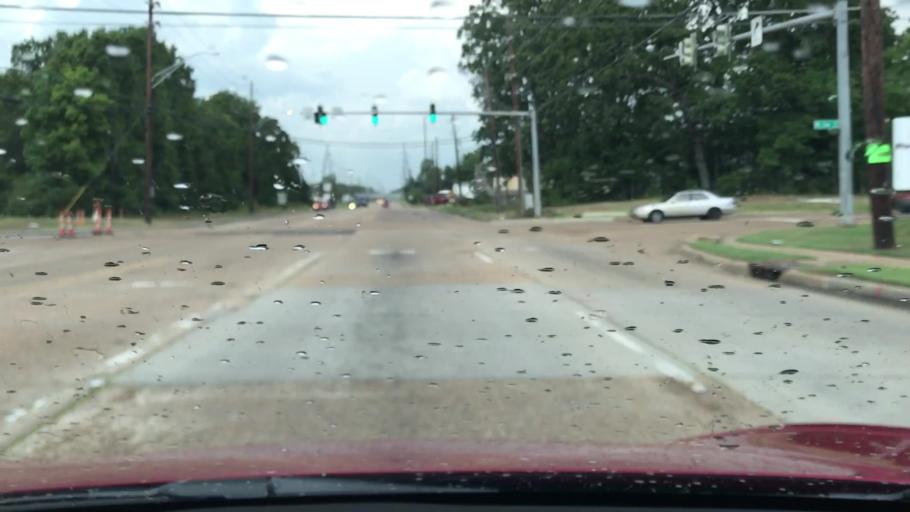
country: US
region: Louisiana
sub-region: Bossier Parish
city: Bossier City
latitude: 32.4127
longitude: -93.7631
